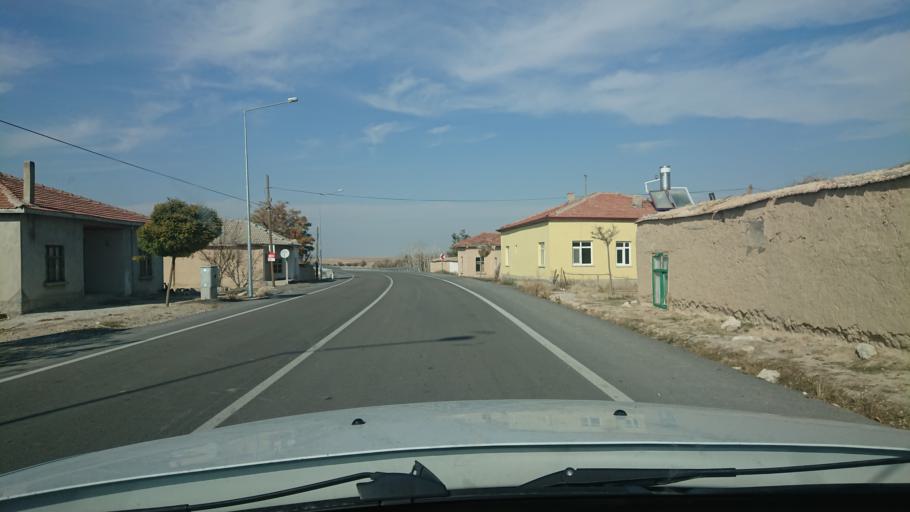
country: TR
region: Aksaray
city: Sultanhani
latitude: 38.2679
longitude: 33.4400
